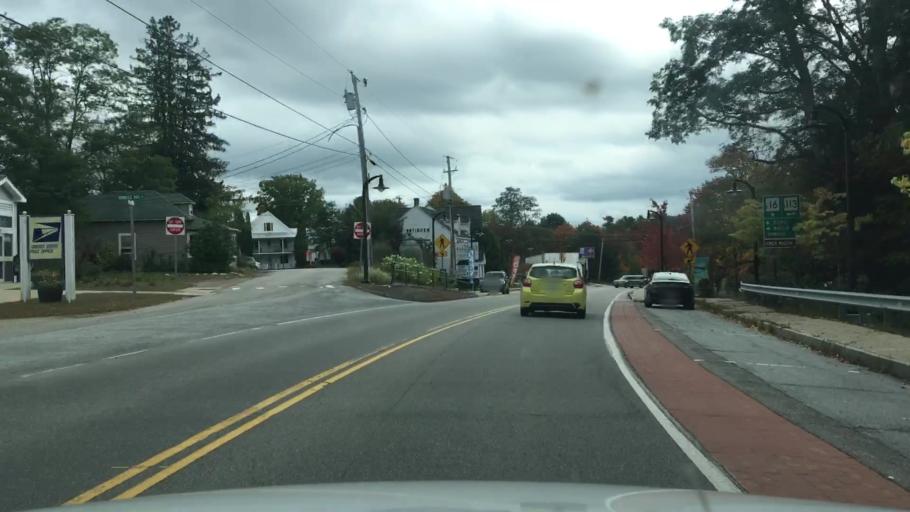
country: US
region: New Hampshire
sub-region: Carroll County
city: Tamworth
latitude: 43.8786
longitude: -71.2210
